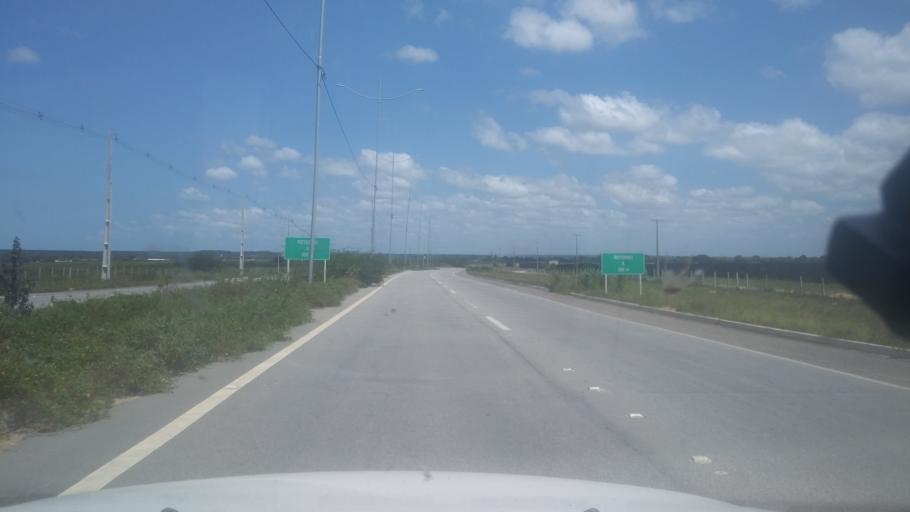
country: BR
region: Rio Grande do Norte
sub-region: Macaiba
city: Macaiba
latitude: -5.8525
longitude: -35.3794
